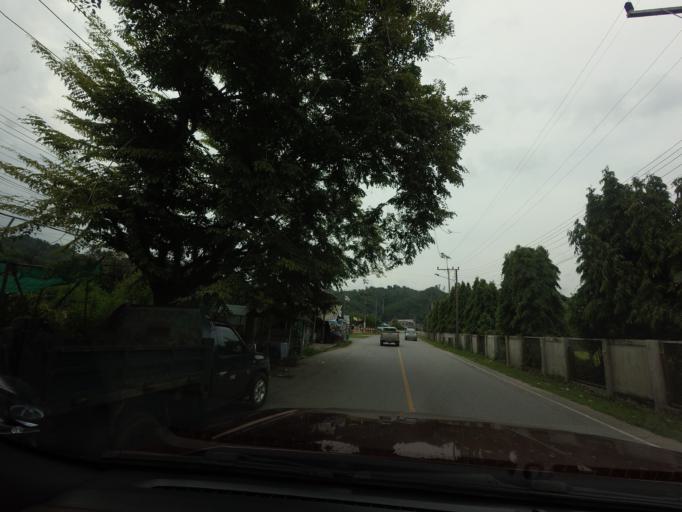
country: TH
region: Yala
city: Than To
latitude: 6.1608
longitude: 101.2747
